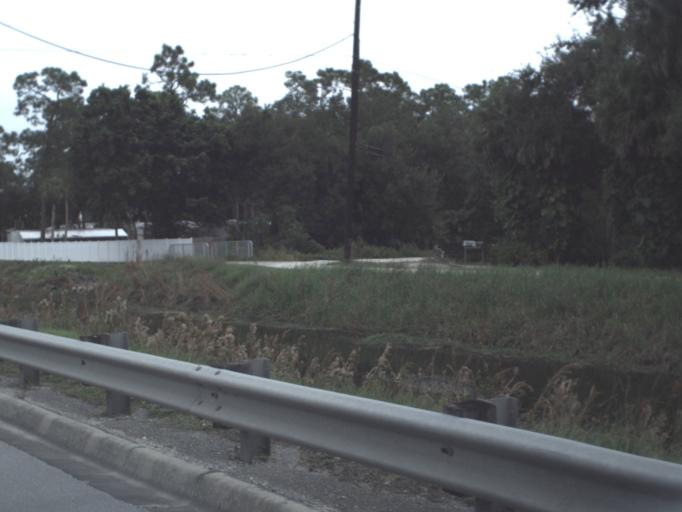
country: US
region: Florida
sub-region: Collier County
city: Lely Resort
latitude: 26.1020
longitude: -81.6871
